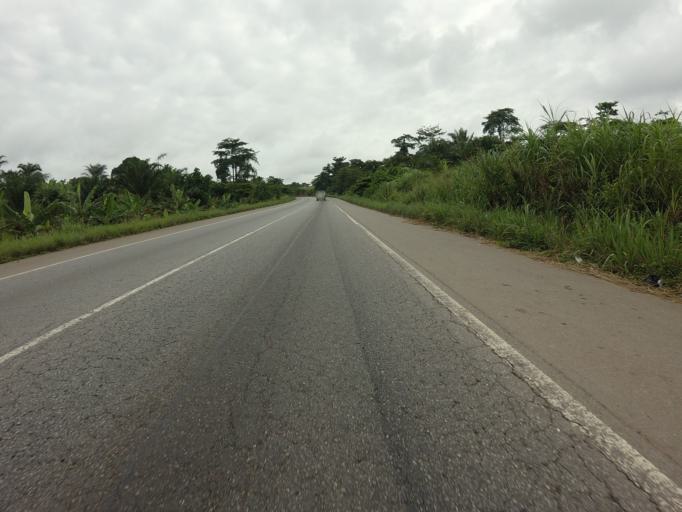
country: GH
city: Bechem
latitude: 7.1072
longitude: -1.7233
